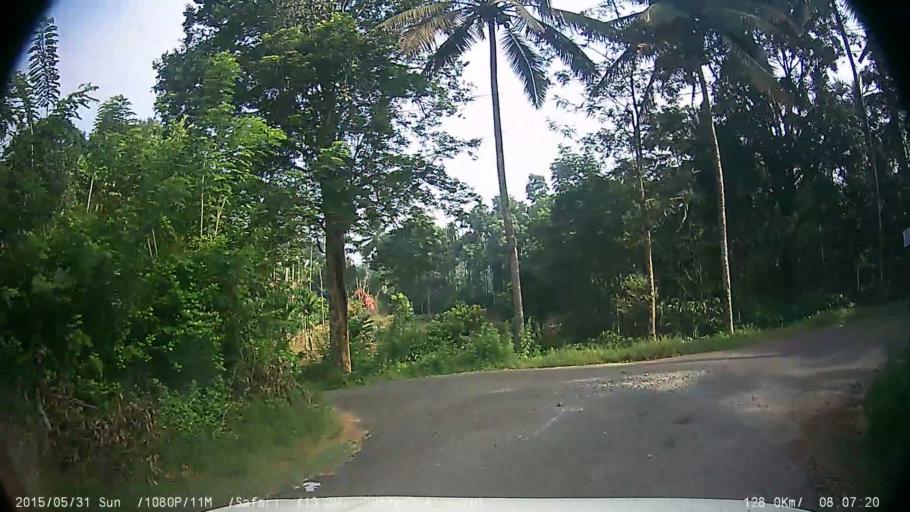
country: IN
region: Kerala
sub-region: Wayanad
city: Kalpetta
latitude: 11.6404
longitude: 76.0292
